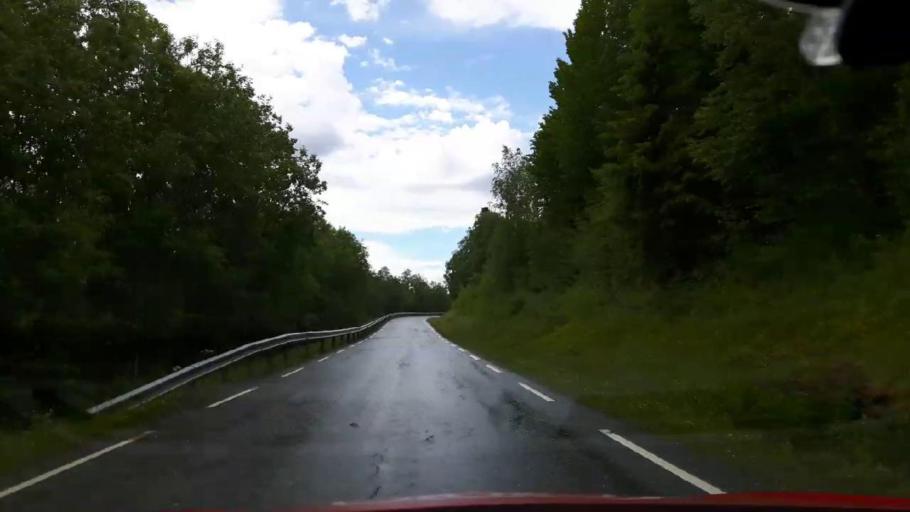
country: NO
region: Nord-Trondelag
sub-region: Lierne
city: Sandvika
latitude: 64.1059
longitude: 13.9896
